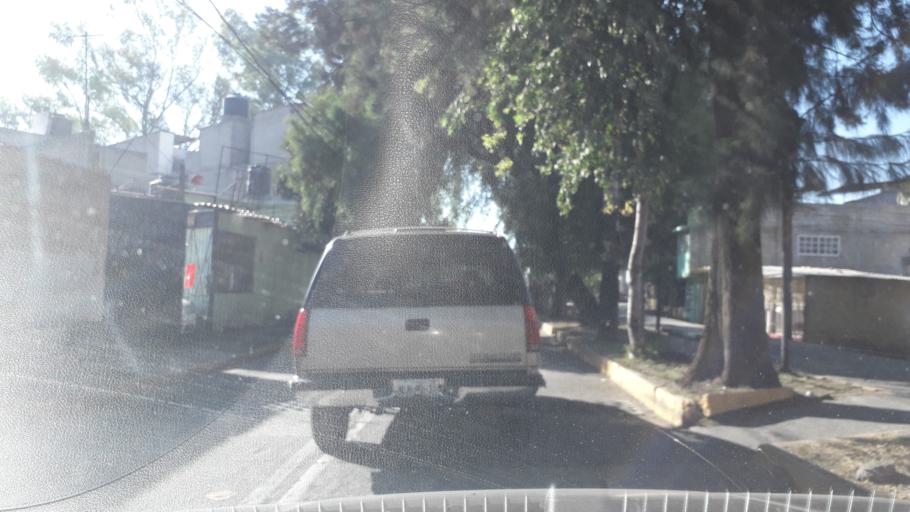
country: MX
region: Mexico City
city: Gustavo A. Madero
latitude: 19.5120
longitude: -99.0899
